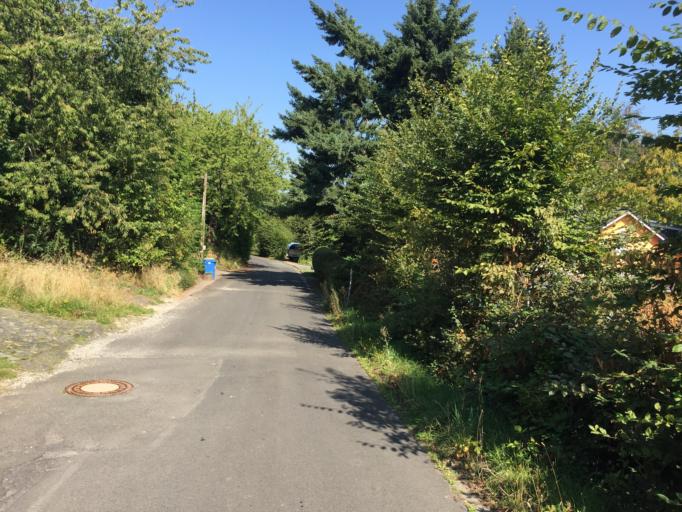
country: DE
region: Hesse
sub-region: Regierungsbezirk Darmstadt
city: Butzbach
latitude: 50.4222
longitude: 8.5938
